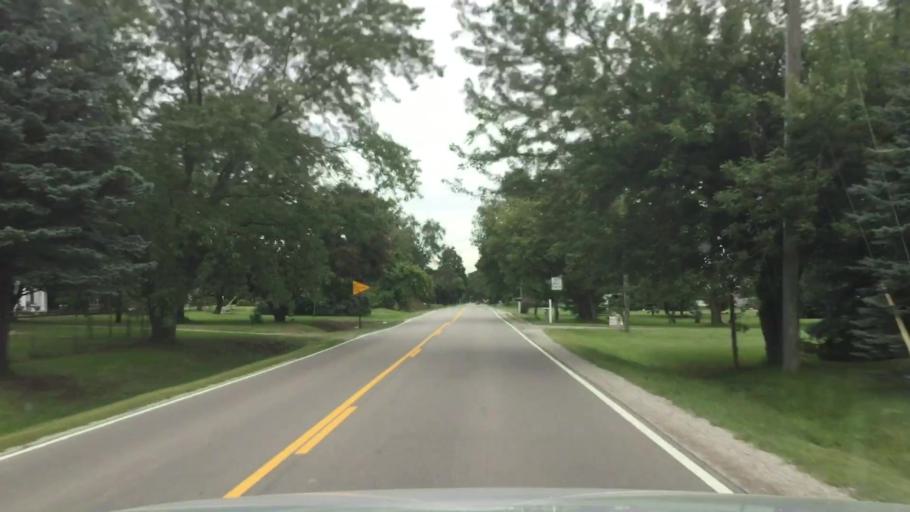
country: US
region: Michigan
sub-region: Washtenaw County
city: Ypsilanti
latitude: 42.1836
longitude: -83.6377
